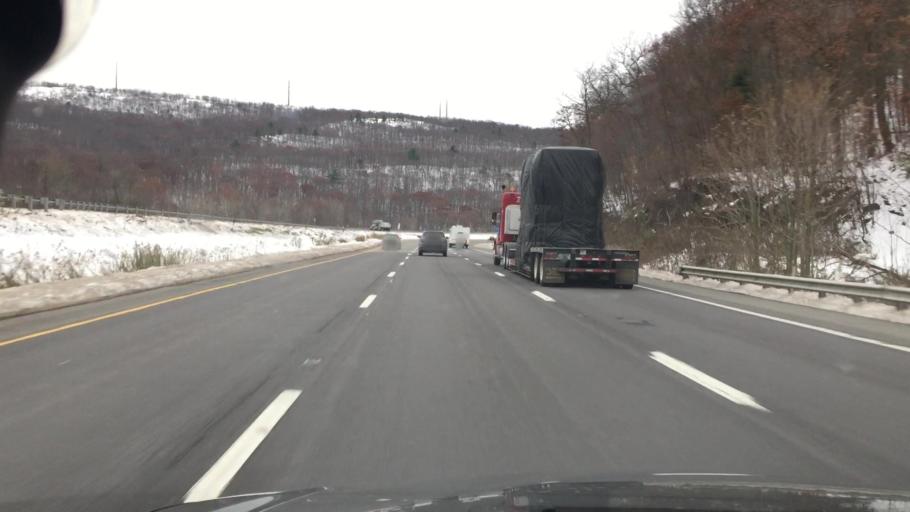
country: US
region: Pennsylvania
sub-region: Luzerne County
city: Ashley
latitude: 41.1913
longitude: -75.9177
